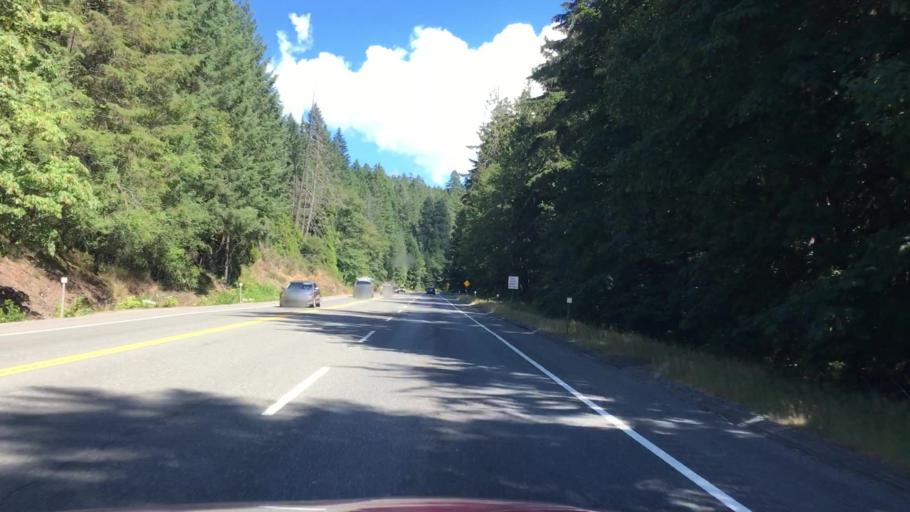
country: CA
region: British Columbia
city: Port Alberni
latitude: 49.2650
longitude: -124.7208
